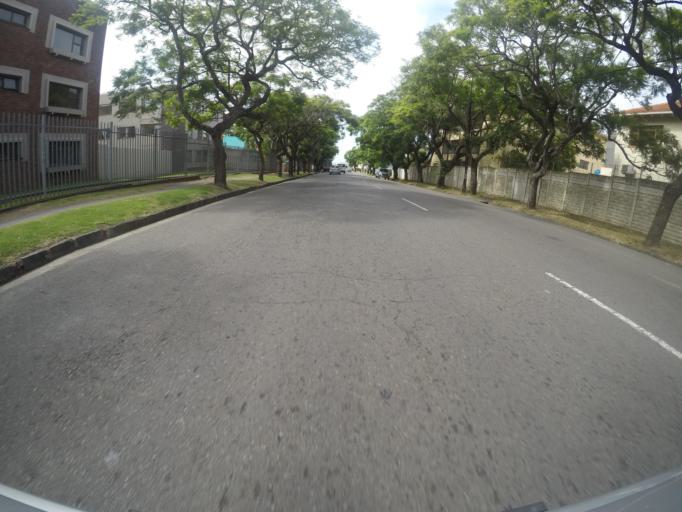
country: ZA
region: Eastern Cape
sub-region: Buffalo City Metropolitan Municipality
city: East London
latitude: -32.9985
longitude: 27.9041
